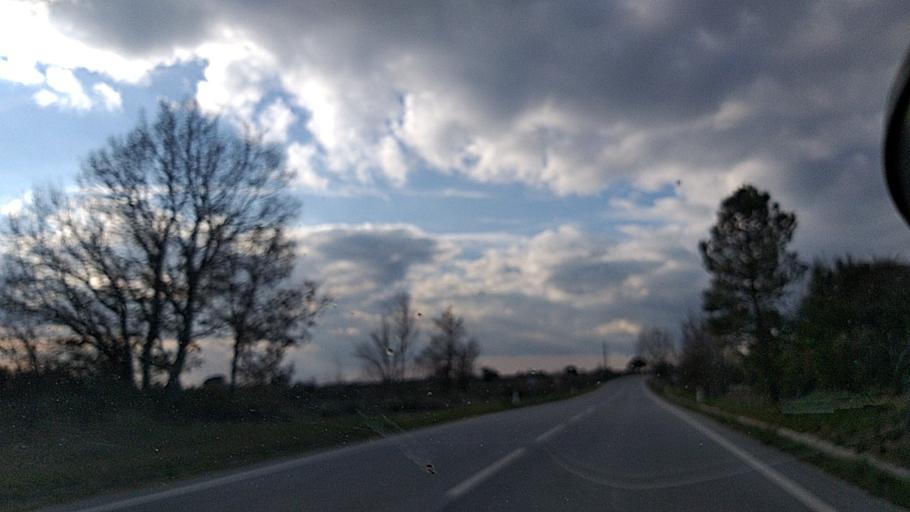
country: ES
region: Castille and Leon
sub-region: Provincia de Salamanca
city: Aldea del Obispo
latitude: 40.6971
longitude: -6.8862
